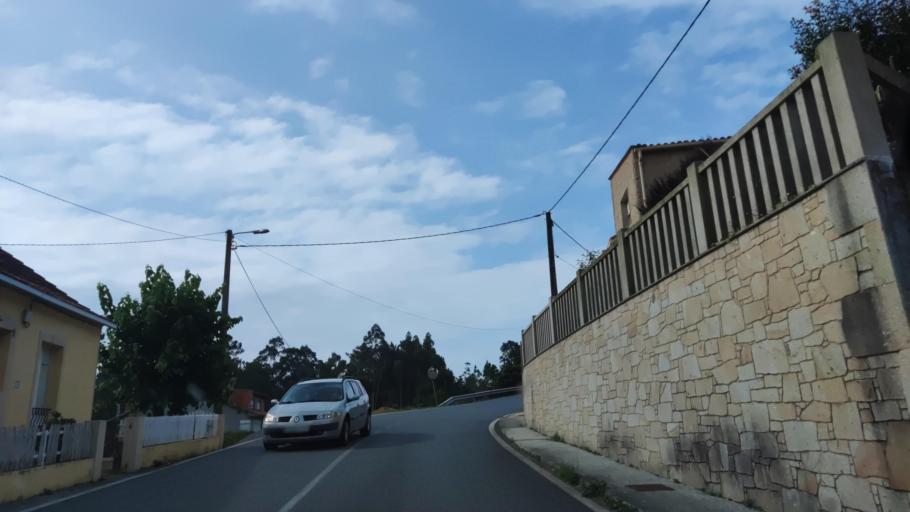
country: ES
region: Galicia
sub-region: Provincia da Coruna
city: Rianxo
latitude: 42.6512
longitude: -8.7791
